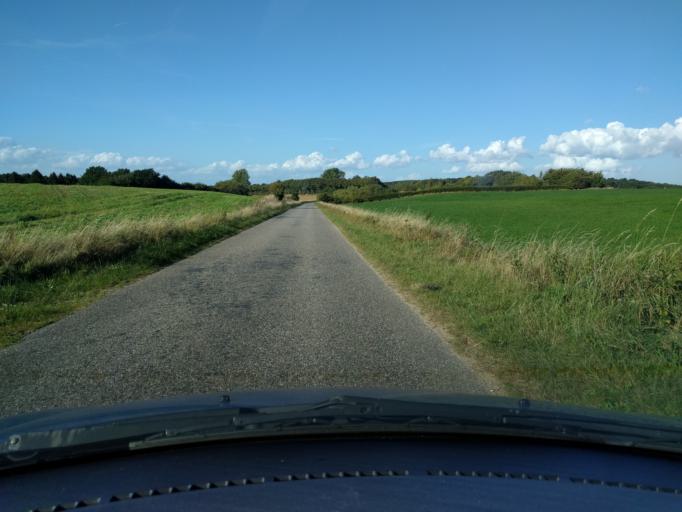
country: DK
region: South Denmark
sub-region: Assens Kommune
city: Harby
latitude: 55.1298
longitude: 10.0316
